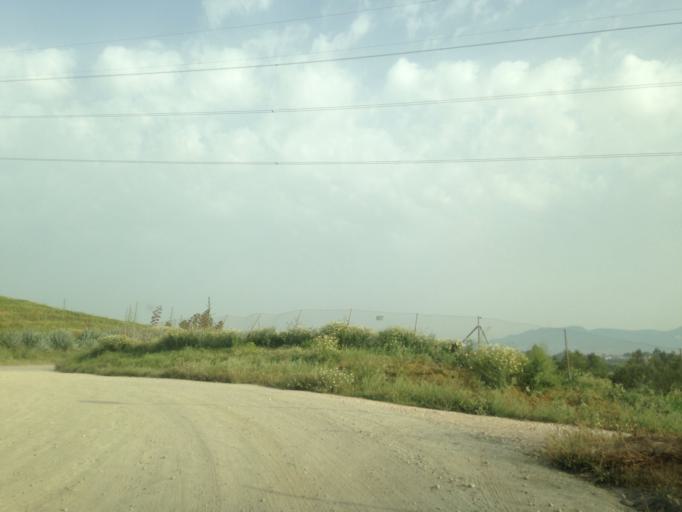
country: ES
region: Andalusia
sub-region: Provincia de Malaga
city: Estacion de Cartama
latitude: 36.7546
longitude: -4.5497
